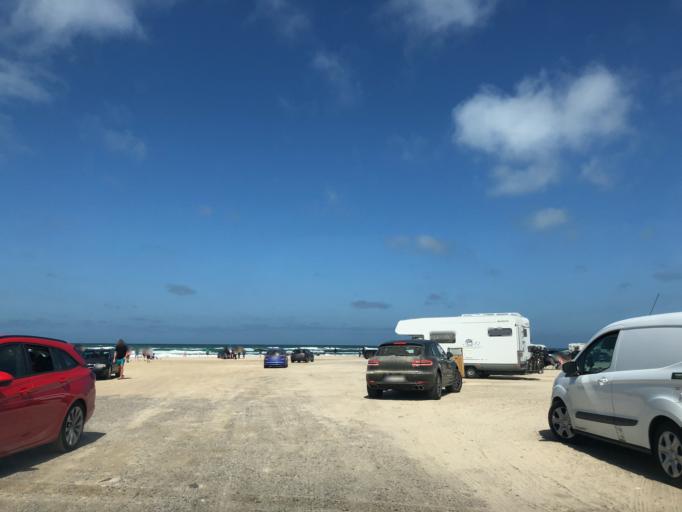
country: DK
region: North Denmark
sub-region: Jammerbugt Kommune
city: Pandrup
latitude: 57.2547
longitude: 9.5804
